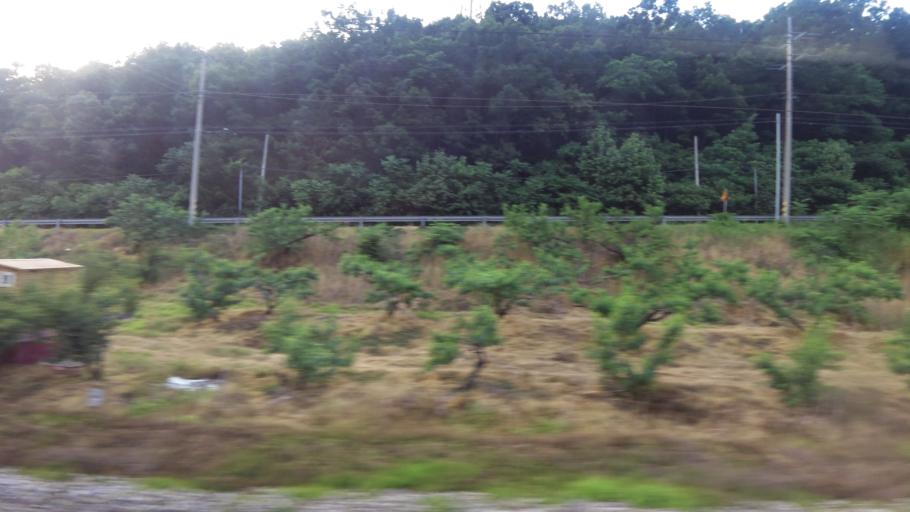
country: KR
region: Chungcheongnam-do
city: Cheonan
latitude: 36.6593
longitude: 127.2298
